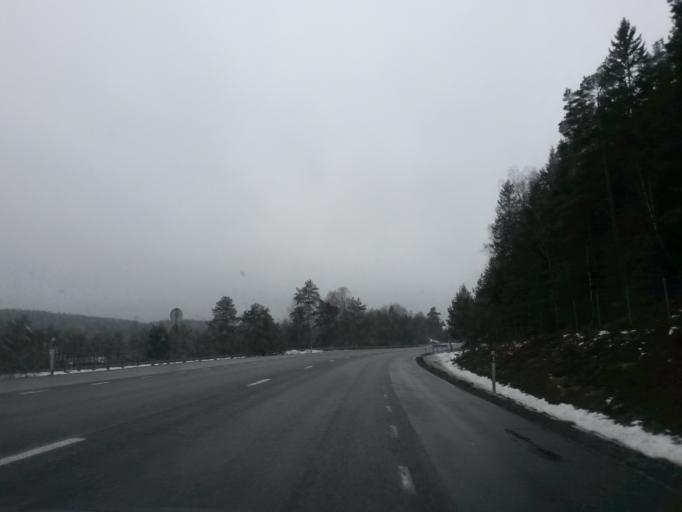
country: SE
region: Vaestra Goetaland
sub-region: Boras Kommun
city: Viskafors
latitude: 57.5778
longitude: 12.8568
